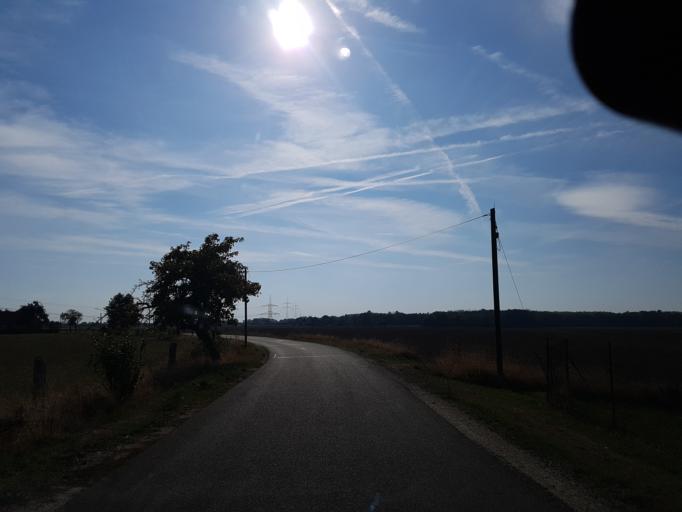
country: DE
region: Brandenburg
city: Doberlug-Kirchhain
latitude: 51.6488
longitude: 13.5445
